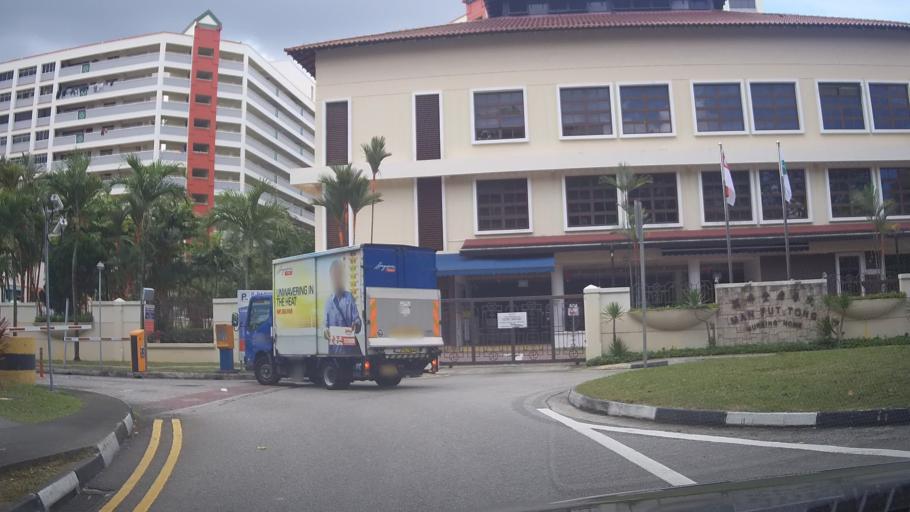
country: MY
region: Johor
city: Johor Bahru
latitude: 1.4435
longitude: 103.7908
